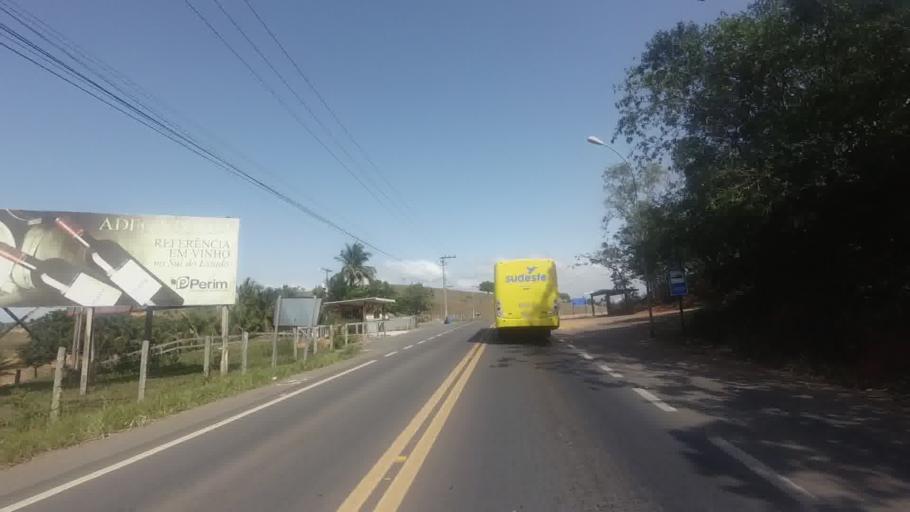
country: BR
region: Espirito Santo
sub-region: Piuma
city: Piuma
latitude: -20.8062
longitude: -40.6682
